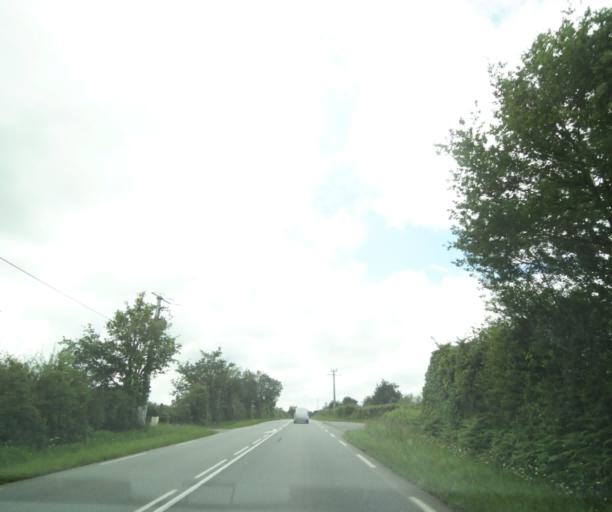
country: FR
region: Poitou-Charentes
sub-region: Departement des Deux-Sevres
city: Viennay
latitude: 46.7012
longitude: -0.2400
